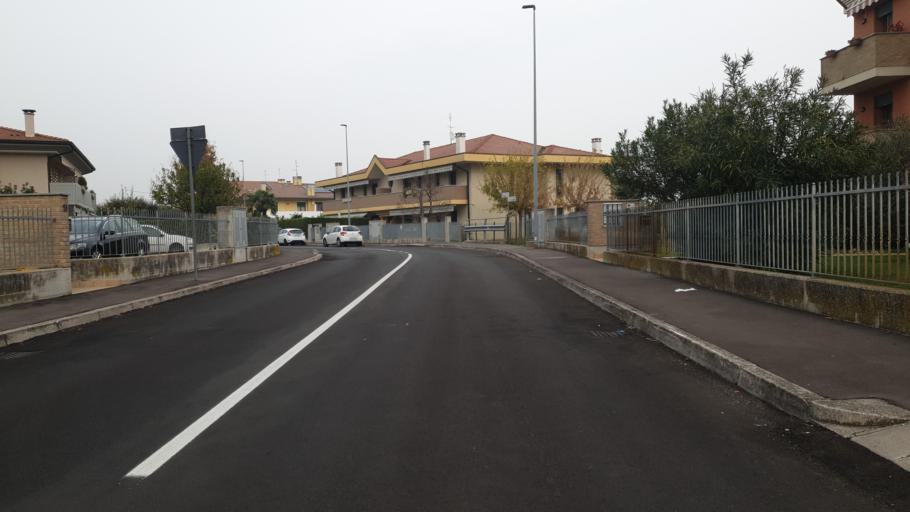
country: IT
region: Veneto
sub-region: Provincia di Padova
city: Bertipaglia
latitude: 45.3124
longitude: 11.8852
